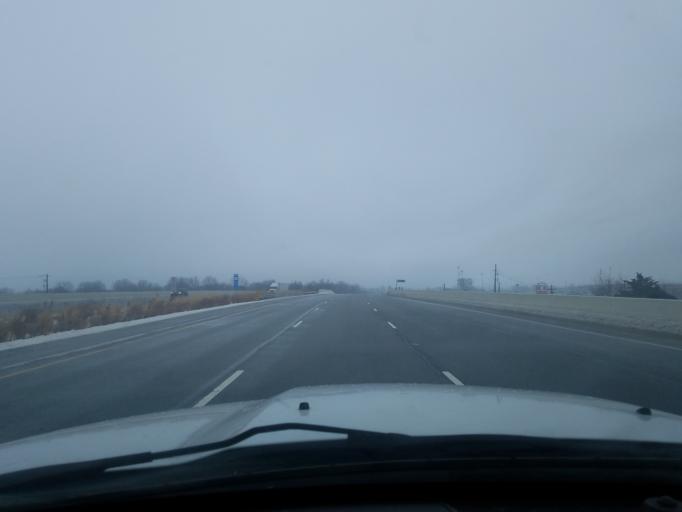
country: US
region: Indiana
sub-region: Hamilton County
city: Westfield
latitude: 40.0487
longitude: -86.1349
